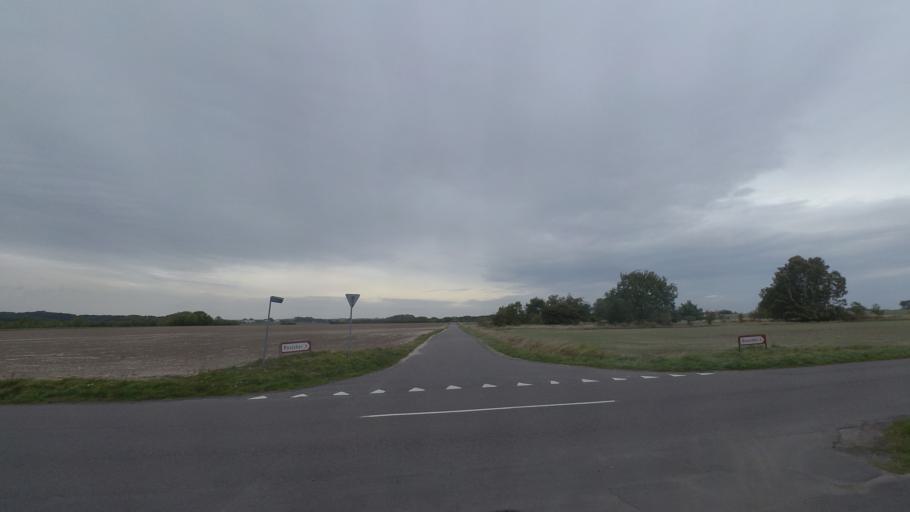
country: DK
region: Capital Region
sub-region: Bornholm Kommune
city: Nexo
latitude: 55.0035
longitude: 15.0380
